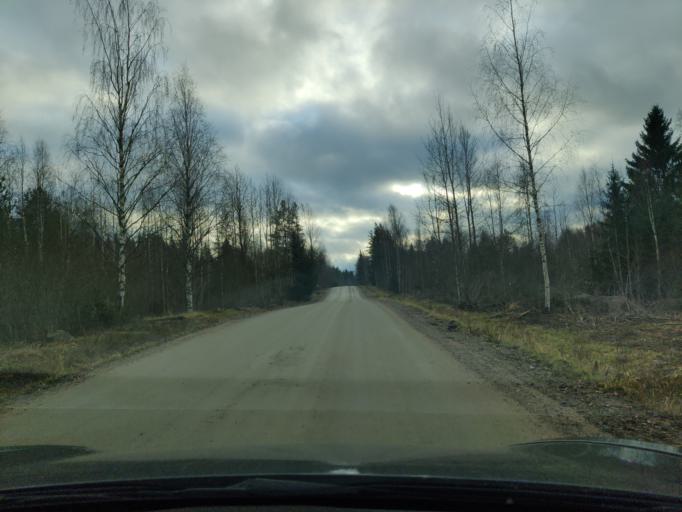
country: FI
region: Northern Savo
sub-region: Ylae-Savo
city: Kiuruvesi
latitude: 63.6403
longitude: 26.6327
